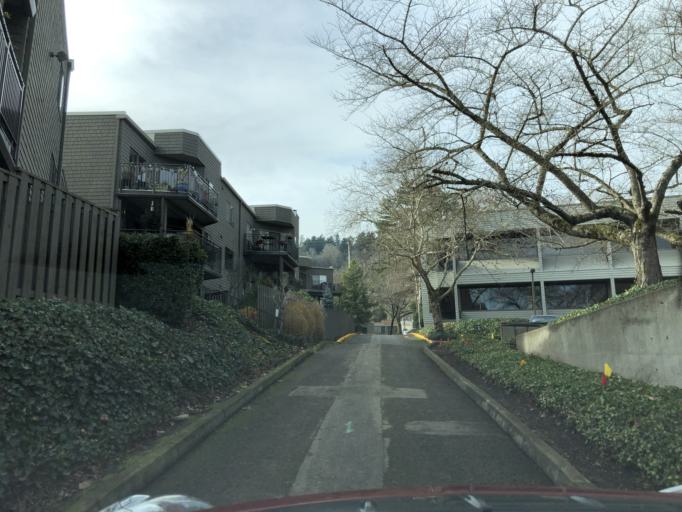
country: US
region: Oregon
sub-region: Multnomah County
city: Portland
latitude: 45.4835
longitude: -122.6729
